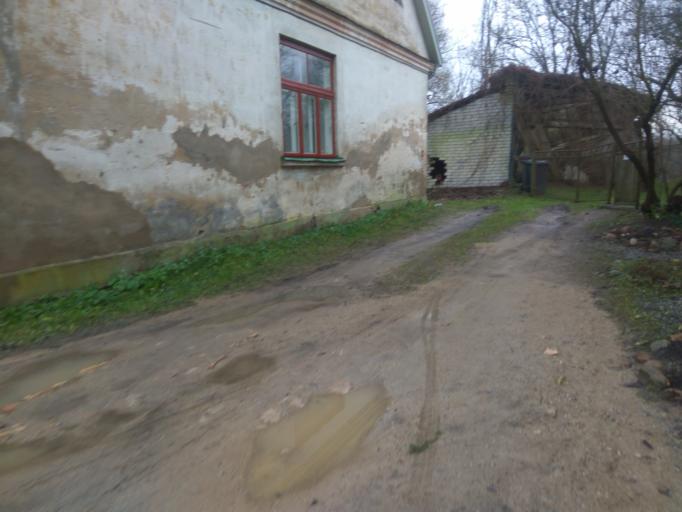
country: LV
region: Kuldigas Rajons
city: Kuldiga
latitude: 56.9677
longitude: 21.9769
